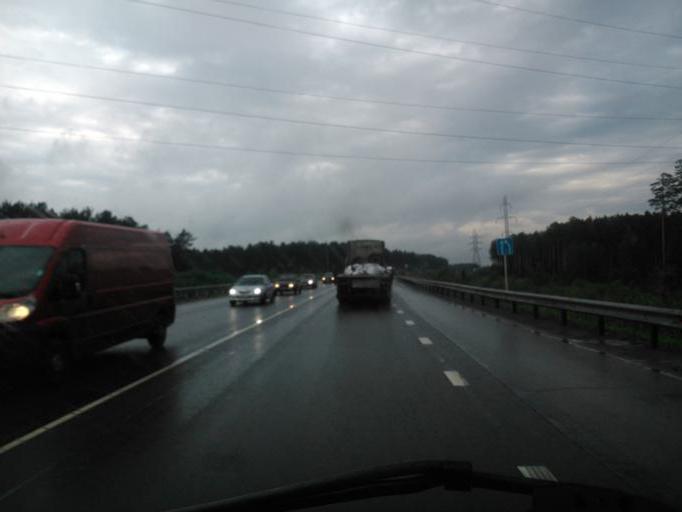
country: RU
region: Sverdlovsk
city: Beryozovsky
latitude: 56.9022
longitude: 60.7578
